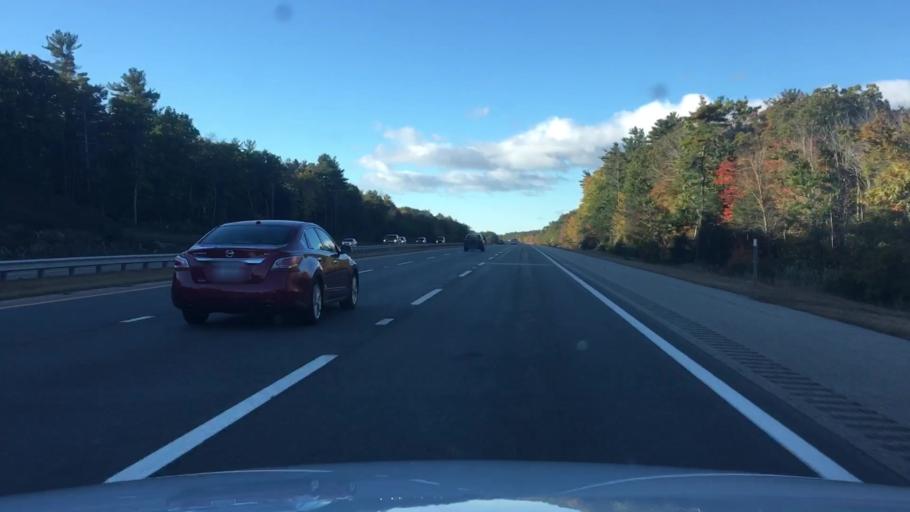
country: US
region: Maine
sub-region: York County
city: Ogunquit
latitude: 43.2477
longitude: -70.6258
